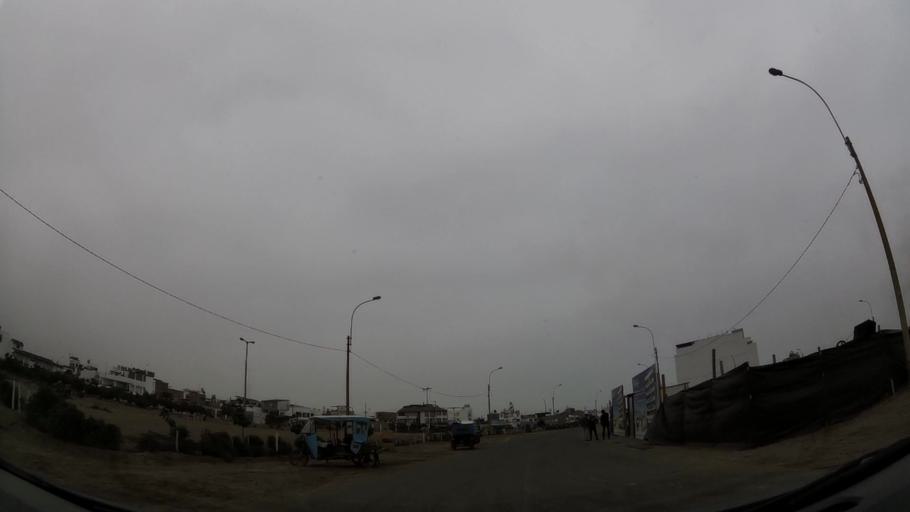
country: PE
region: Lima
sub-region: Lima
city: Punta Hermosa
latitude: -12.3291
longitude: -76.8305
